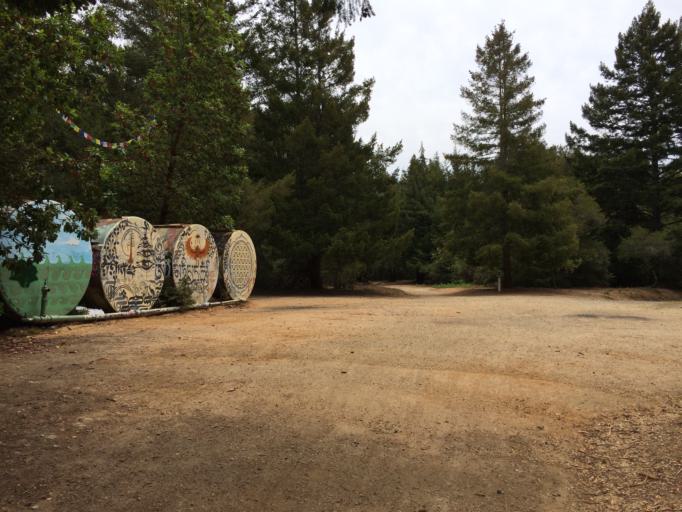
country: US
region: California
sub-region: Santa Cruz County
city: Pasatiempo
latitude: 37.0101
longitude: -122.0665
